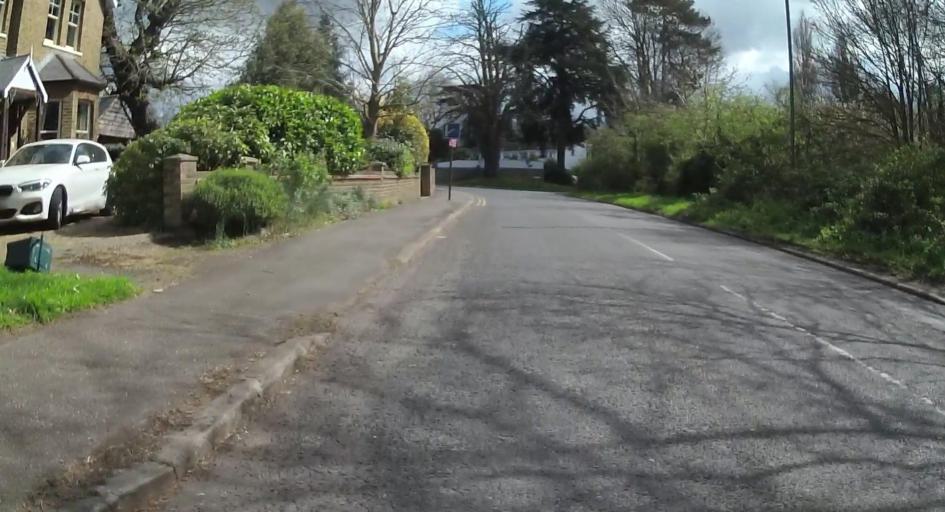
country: GB
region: England
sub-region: Surrey
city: Shepperton
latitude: 51.3880
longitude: -0.4588
